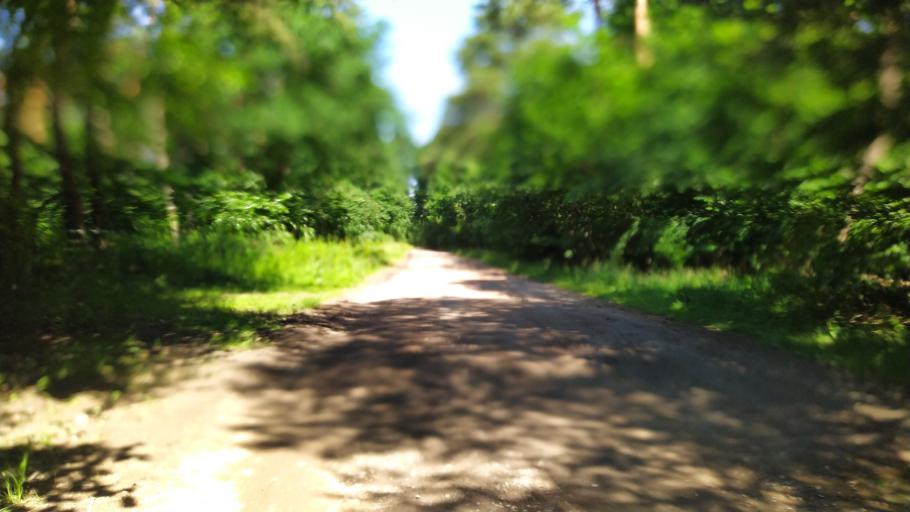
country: DE
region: Lower Saxony
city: Deinste
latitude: 53.5008
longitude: 9.4417
